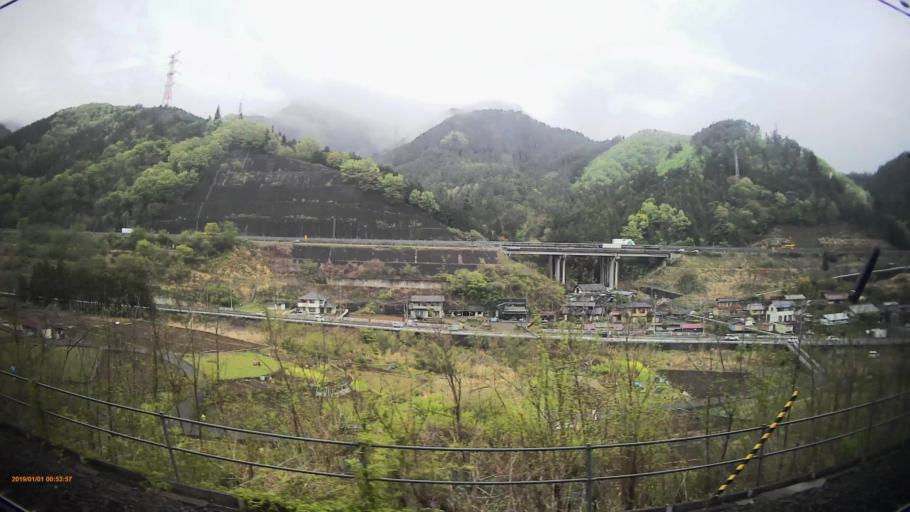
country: JP
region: Yamanashi
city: Otsuki
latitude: 35.6010
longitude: 138.8633
